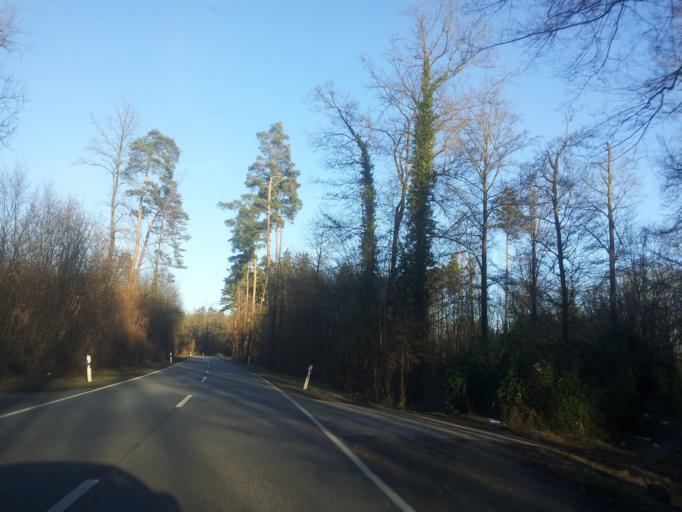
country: DE
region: Baden-Wuerttemberg
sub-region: Regierungsbezirk Stuttgart
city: Flein
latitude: 49.0859
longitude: 9.2343
